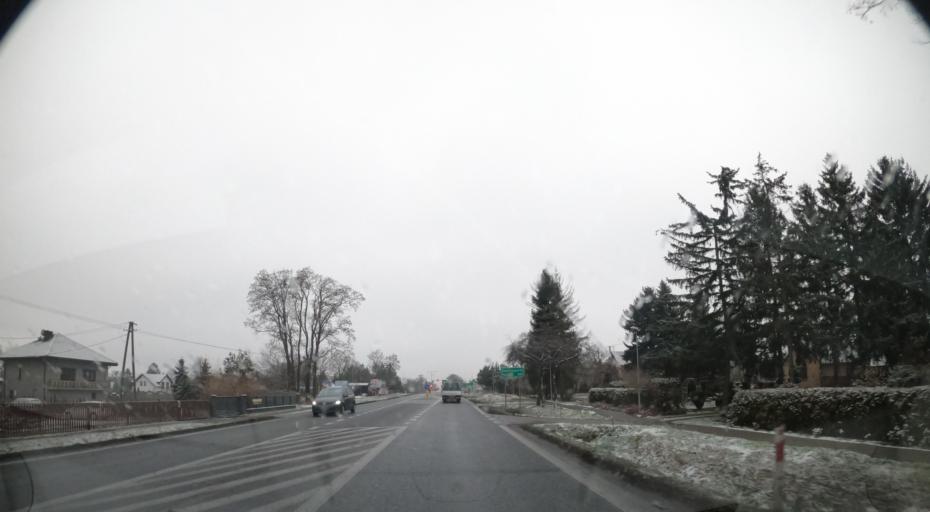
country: PL
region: Masovian Voivodeship
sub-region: Powiat sochaczewski
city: Paprotnia
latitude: 52.2130
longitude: 20.4189
